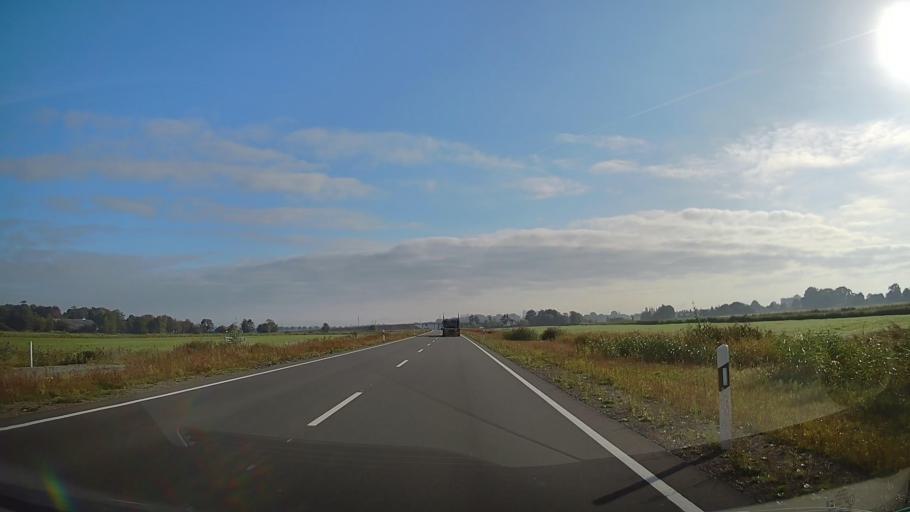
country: DE
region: Lower Saxony
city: Ovelgonne
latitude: 53.3258
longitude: 8.4359
